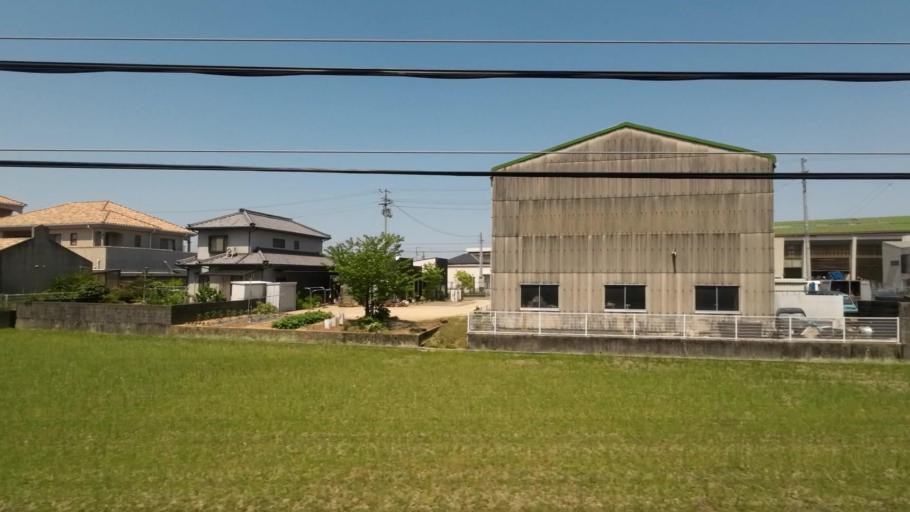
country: JP
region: Ehime
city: Hojo
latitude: 34.0375
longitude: 132.8463
